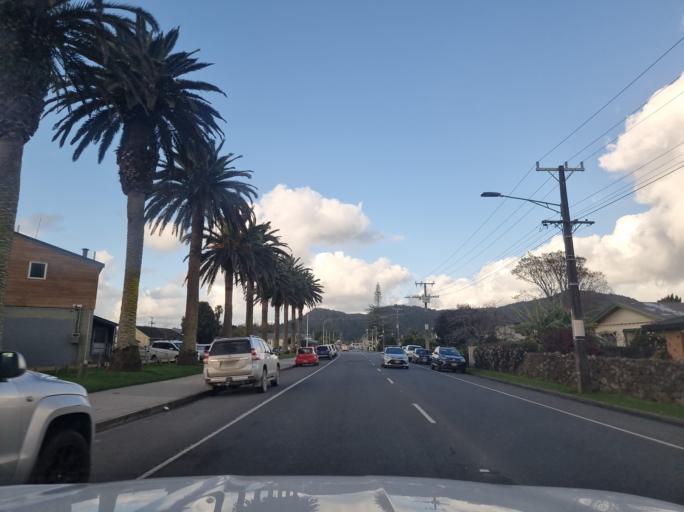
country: NZ
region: Northland
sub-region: Whangarei
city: Whangarei
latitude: -35.7096
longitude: 174.3163
